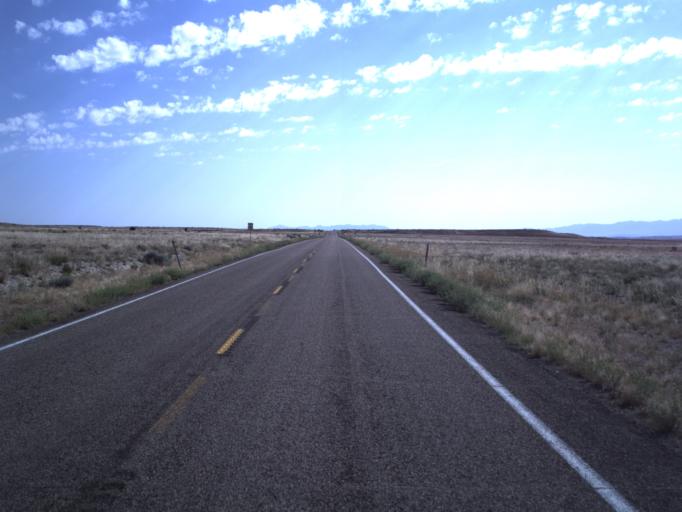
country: US
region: Utah
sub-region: Beaver County
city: Milford
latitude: 38.8173
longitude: -112.8616
